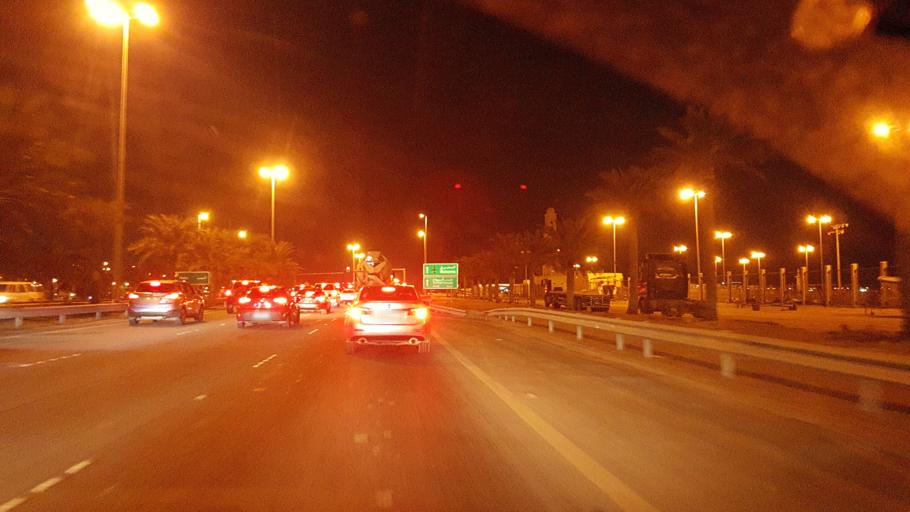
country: BH
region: Muharraq
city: Al Hadd
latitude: 26.2430
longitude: 50.6583
